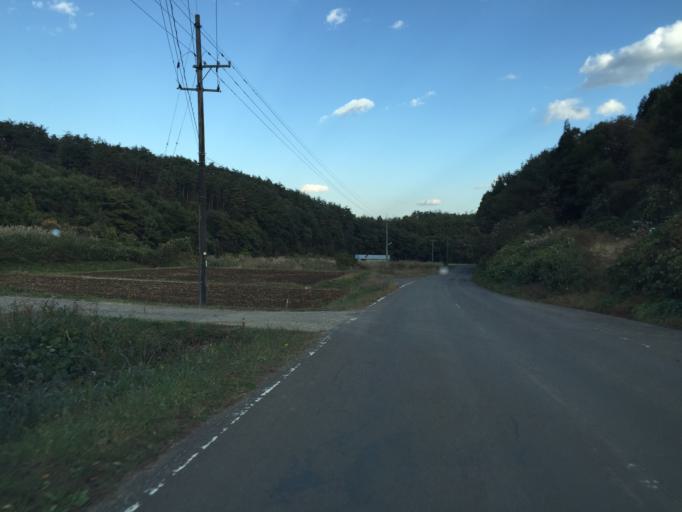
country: JP
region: Fukushima
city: Fukushima-shi
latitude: 37.7058
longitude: 140.4013
